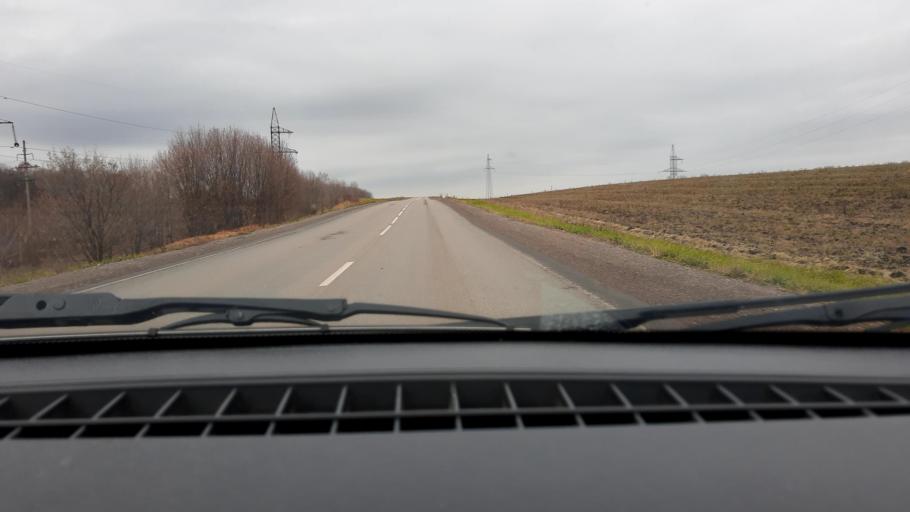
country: RU
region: Bashkortostan
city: Mikhaylovka
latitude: 54.8306
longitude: 55.8952
